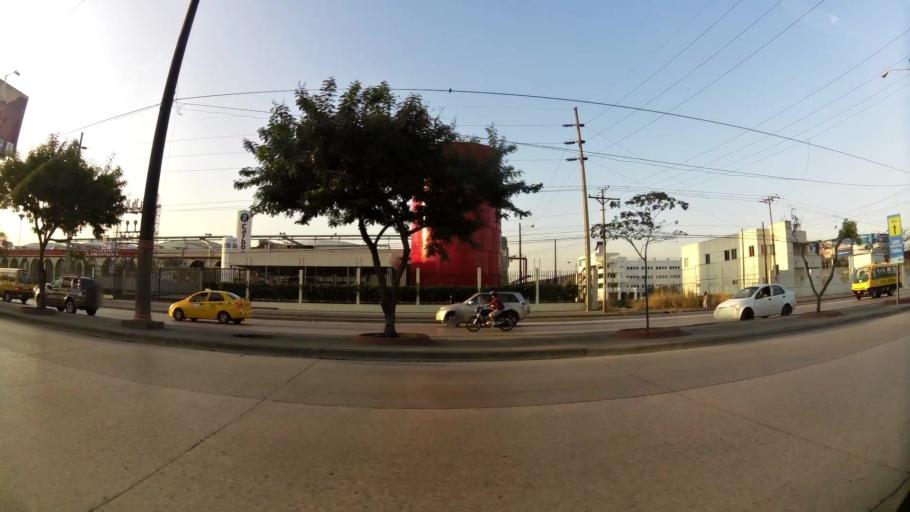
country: EC
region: Guayas
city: Guayaquil
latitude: -2.1450
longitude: -79.9163
